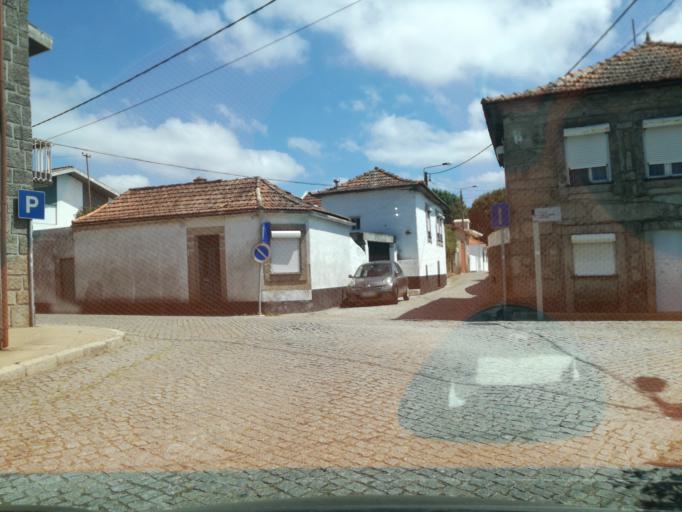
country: PT
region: Porto
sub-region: Maia
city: Maia
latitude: 41.2452
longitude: -8.6070
